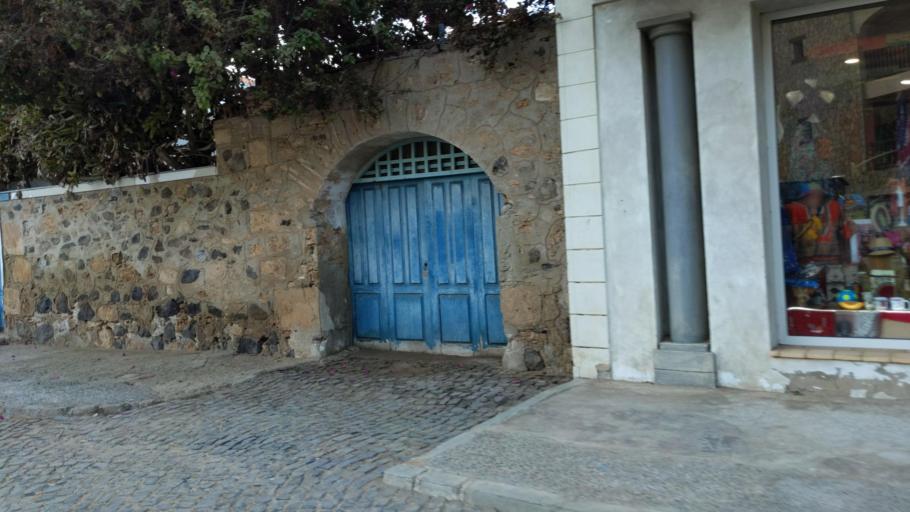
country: CV
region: Sal
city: Santa Maria
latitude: 16.5979
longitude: -22.9047
